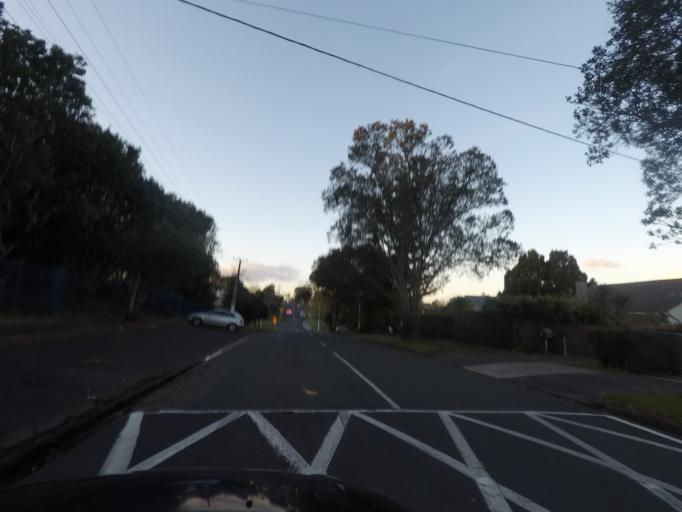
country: NZ
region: Auckland
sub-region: Auckland
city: Waitakere
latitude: -36.9080
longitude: 174.6668
